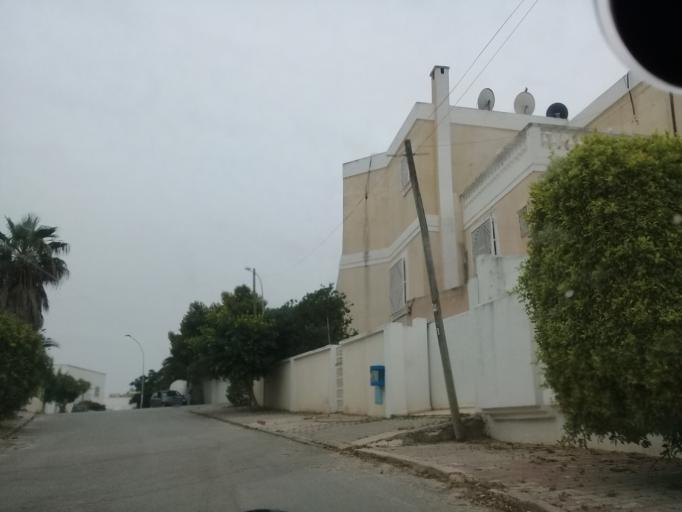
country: TN
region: Tunis
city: Tunis
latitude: 36.8460
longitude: 10.1485
